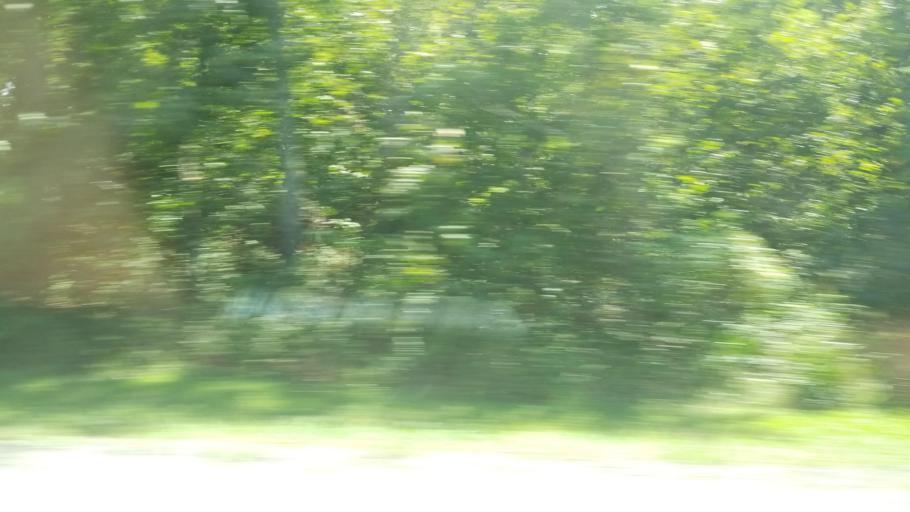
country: US
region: Illinois
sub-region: Williamson County
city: Johnston City
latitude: 37.7903
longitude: -88.8269
